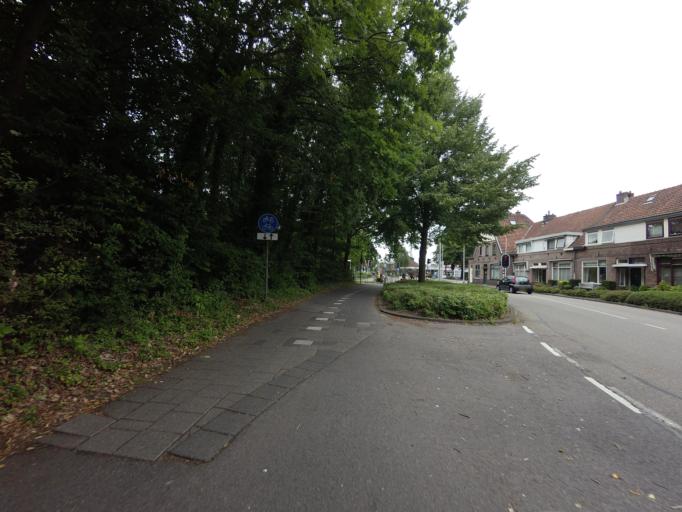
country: NL
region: South Holland
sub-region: Gemeente Oegstgeest
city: Oegstgeest
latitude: 52.1917
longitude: 4.4960
